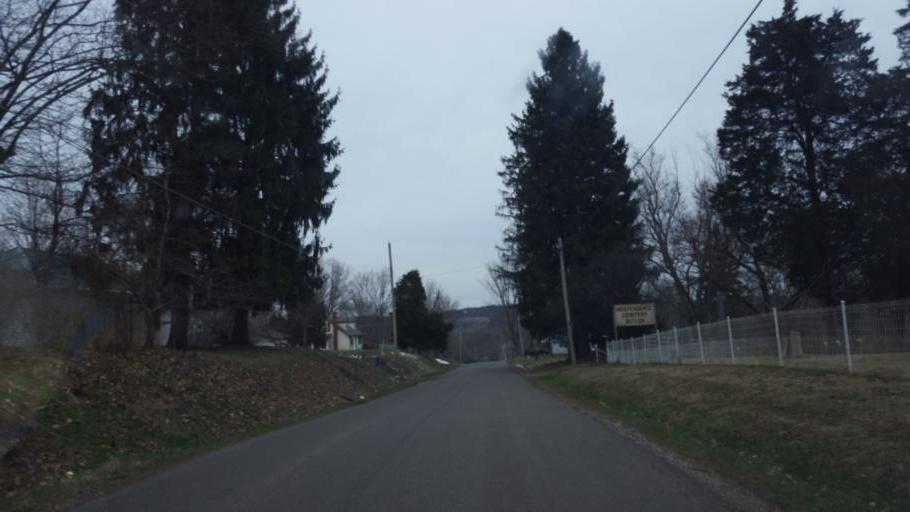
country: US
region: Ohio
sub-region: Sandusky County
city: Bellville
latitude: 40.5835
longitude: -82.4238
